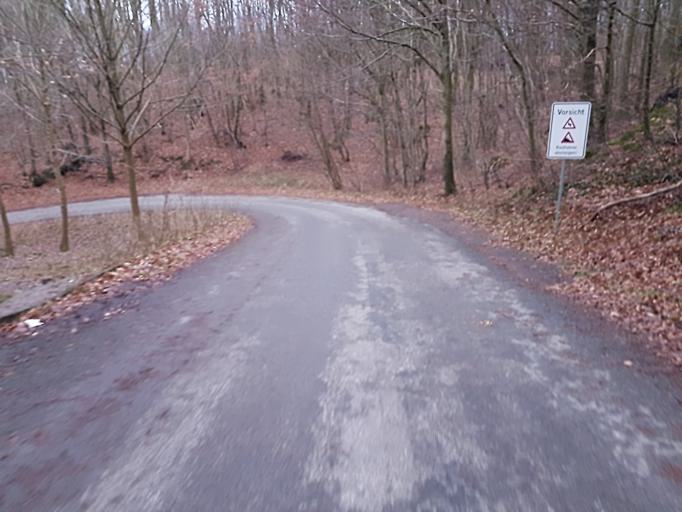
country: DE
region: Mecklenburg-Vorpommern
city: Ostseebad Binz
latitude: 54.3826
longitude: 13.6292
